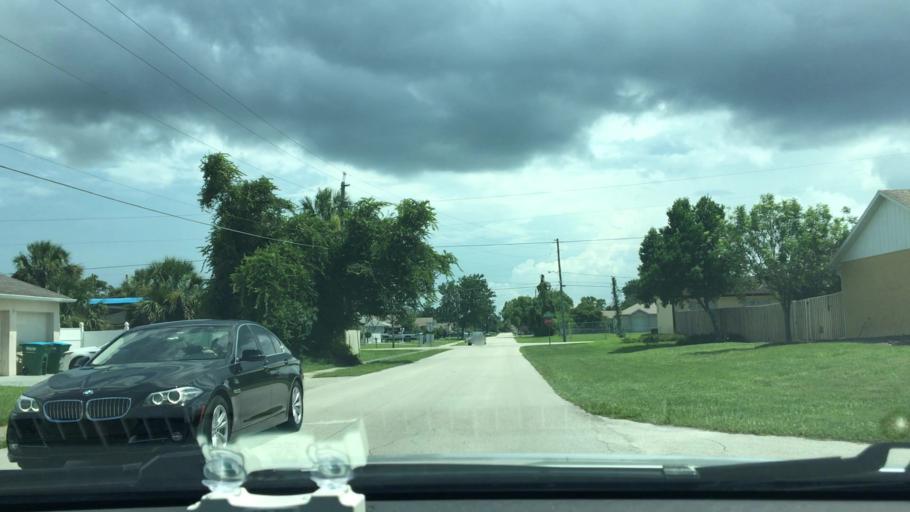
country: US
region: Florida
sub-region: Volusia County
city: Deltona
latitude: 28.8810
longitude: -81.2325
